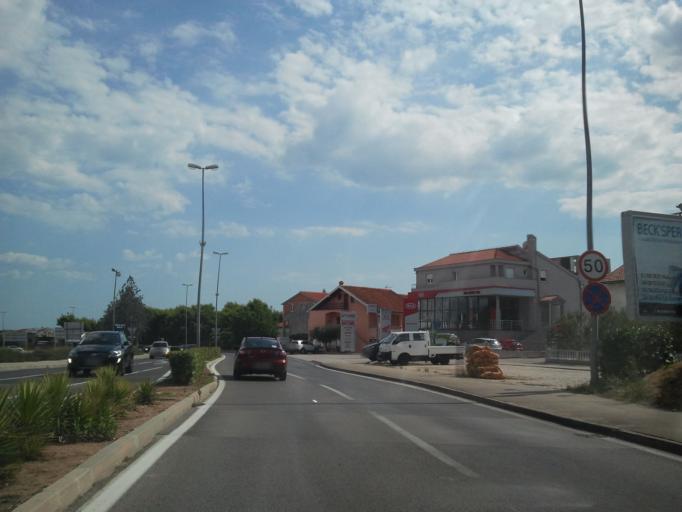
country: HR
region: Zadarska
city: Zadar
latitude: 44.1138
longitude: 15.2542
